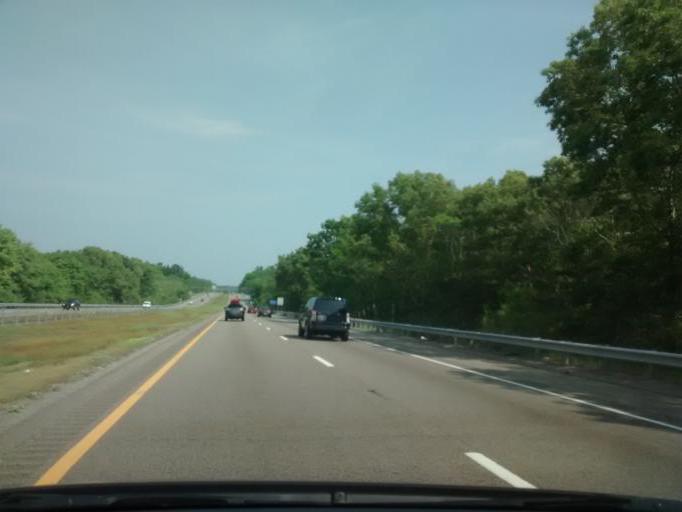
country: US
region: Massachusetts
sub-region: Plymouth County
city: Middleborough Center
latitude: 41.8800
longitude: -70.9152
